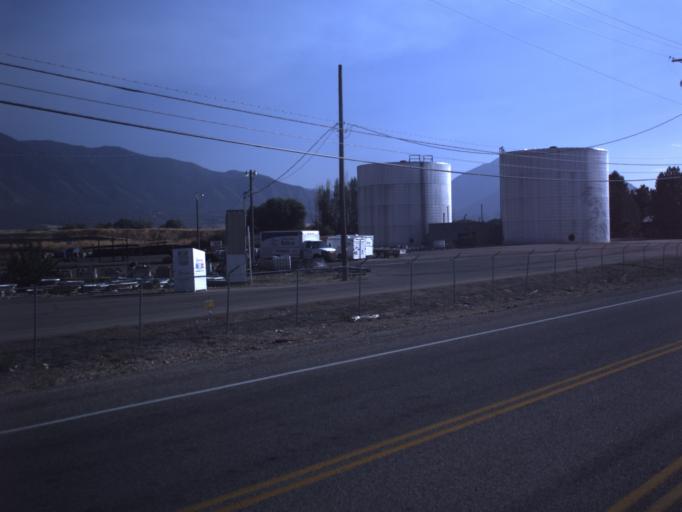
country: US
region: Utah
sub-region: Utah County
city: Spanish Fork
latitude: 40.0922
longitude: -111.6593
